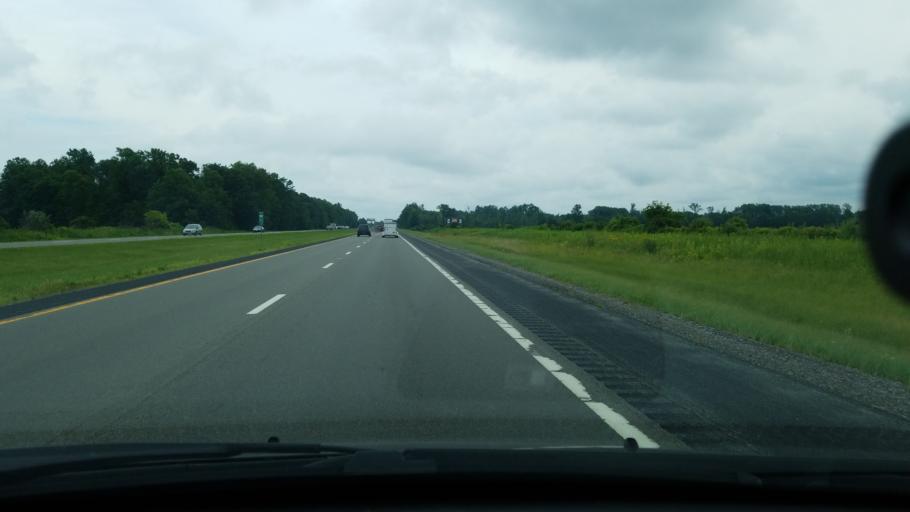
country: US
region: Ohio
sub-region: Lorain County
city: Vermilion
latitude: 41.3908
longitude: -82.4036
